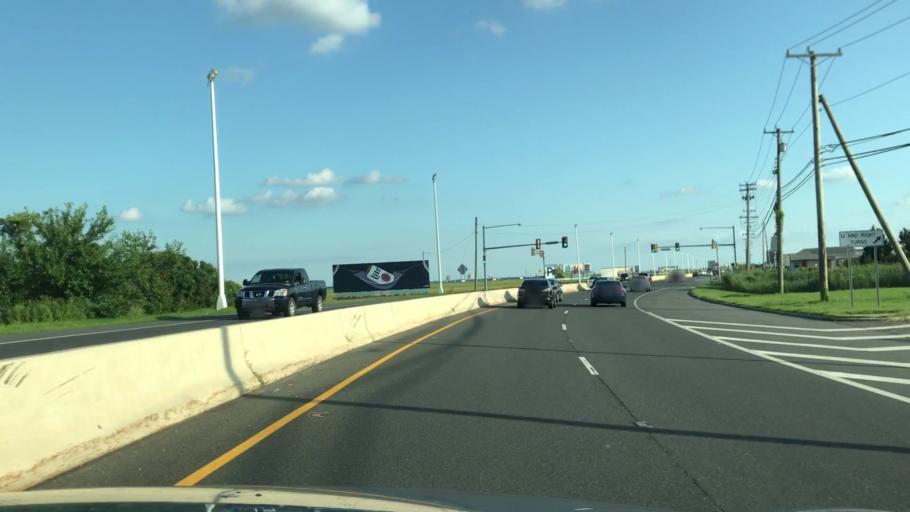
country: US
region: New Jersey
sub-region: Atlantic County
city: Absecon
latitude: 39.4163
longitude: -74.4914
